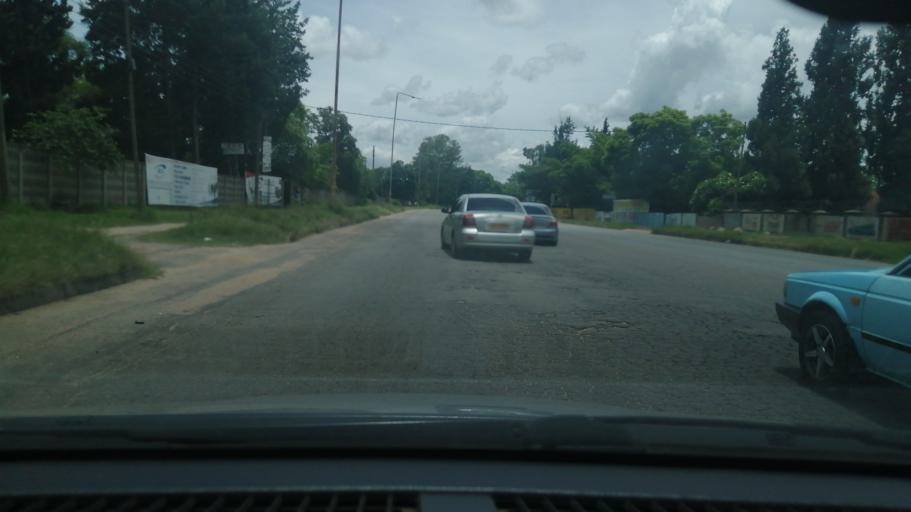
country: ZW
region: Harare
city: Harare
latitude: -17.8755
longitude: 31.0675
